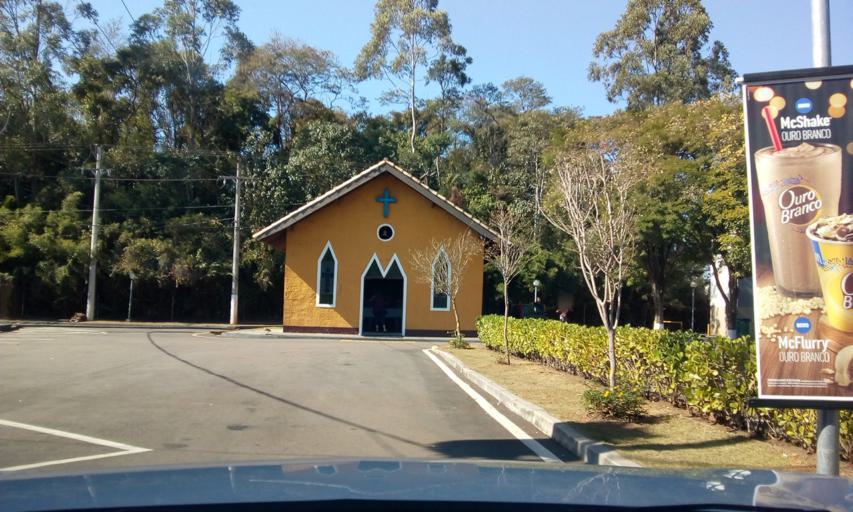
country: BR
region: Sao Paulo
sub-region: Jundiai
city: Jundiai
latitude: -23.1885
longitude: -46.9308
